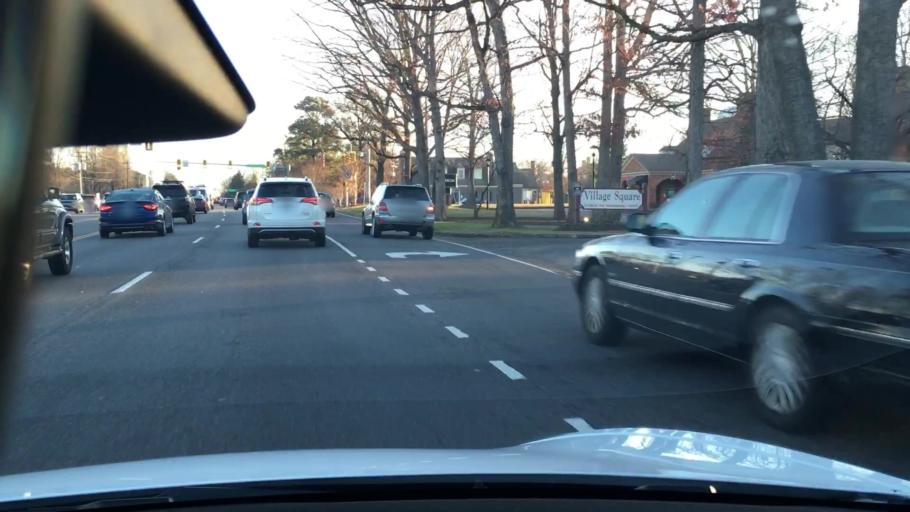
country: US
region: Virginia
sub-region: Chesterfield County
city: Bon Air
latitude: 37.5356
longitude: -77.5656
